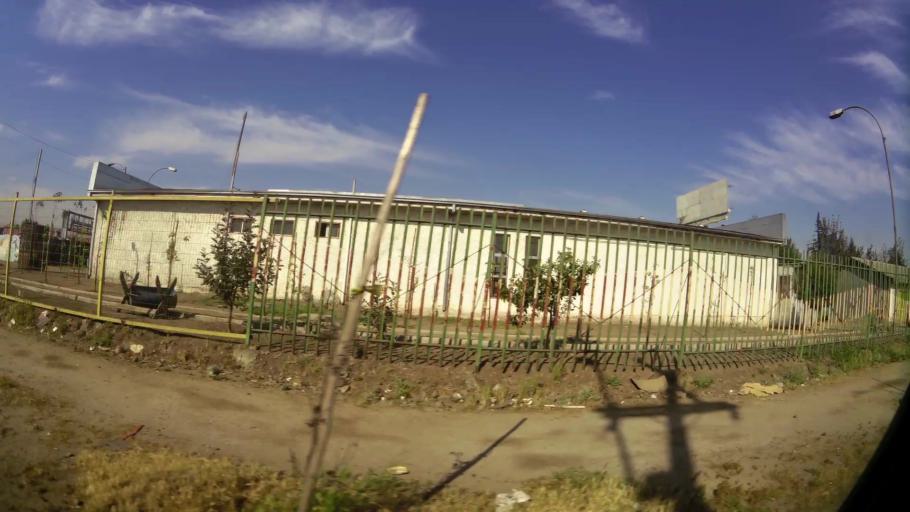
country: CL
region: Santiago Metropolitan
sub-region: Provincia de Maipo
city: San Bernardo
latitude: -33.5254
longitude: -70.6942
